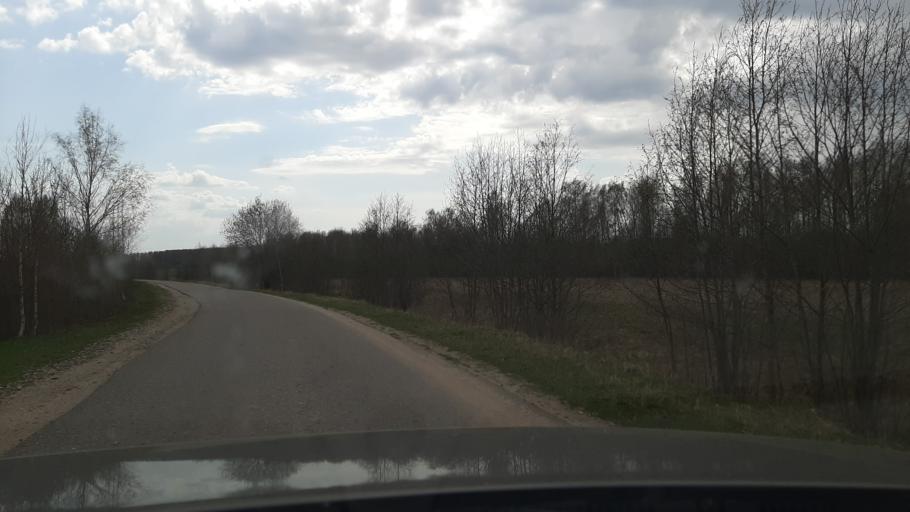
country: RU
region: Ivanovo
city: Furmanov
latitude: 57.3094
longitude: 41.1620
